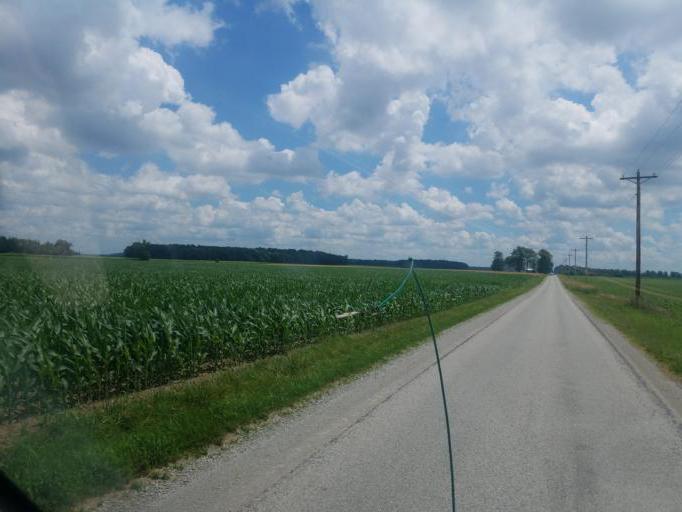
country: US
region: Ohio
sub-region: Huron County
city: Willard
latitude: 41.0276
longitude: -82.8307
